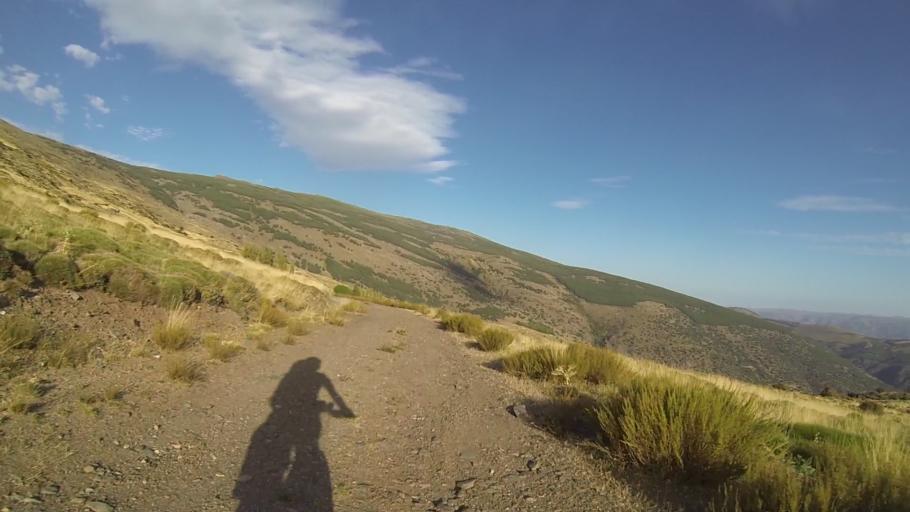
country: ES
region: Andalusia
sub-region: Provincia de Almeria
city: Laujar de Andarax
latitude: 37.0711
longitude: -2.8898
